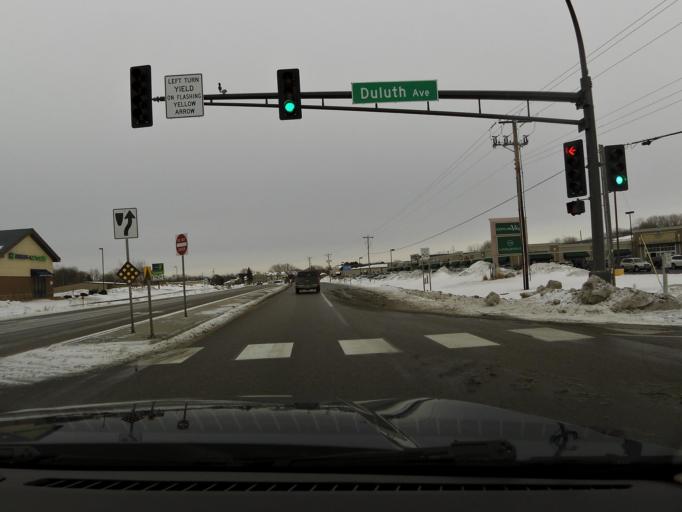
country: US
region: Minnesota
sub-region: Scott County
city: Prior Lake
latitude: 44.7077
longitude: -93.4290
